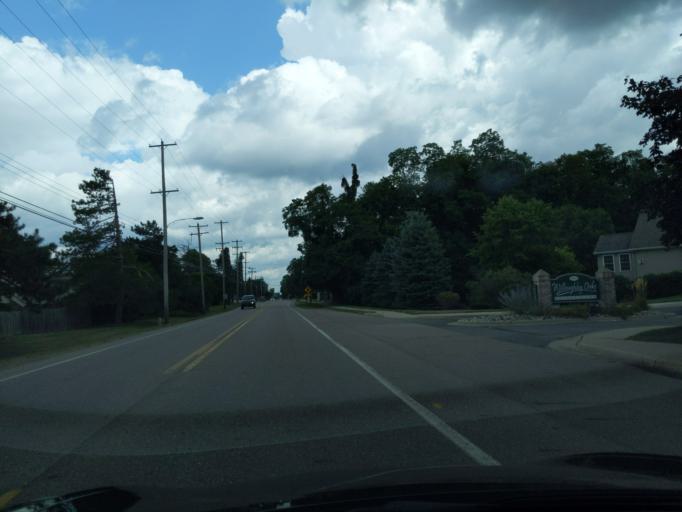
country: US
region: Michigan
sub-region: Ingham County
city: Holt
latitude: 42.6548
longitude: -84.5456
